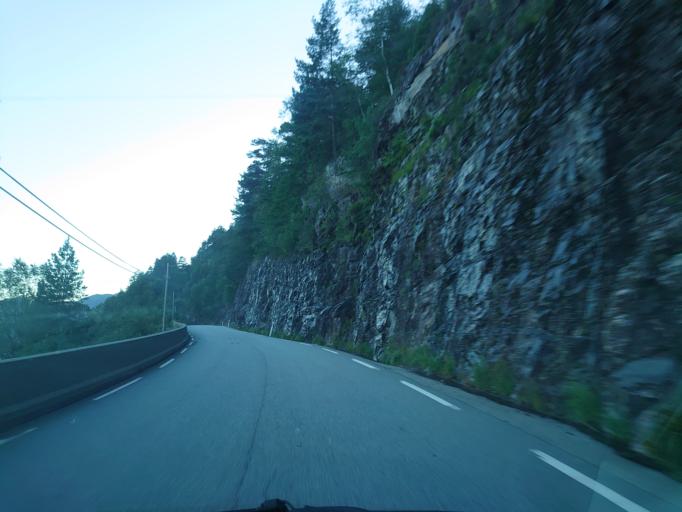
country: NO
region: Hordaland
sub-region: Osteroy
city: Lonevag
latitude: 60.7087
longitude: 5.6115
